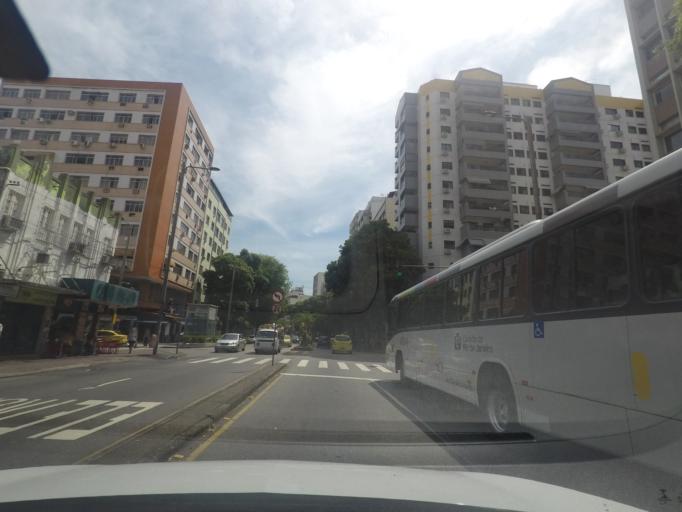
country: BR
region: Rio de Janeiro
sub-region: Rio De Janeiro
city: Rio de Janeiro
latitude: -22.9320
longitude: -43.2399
